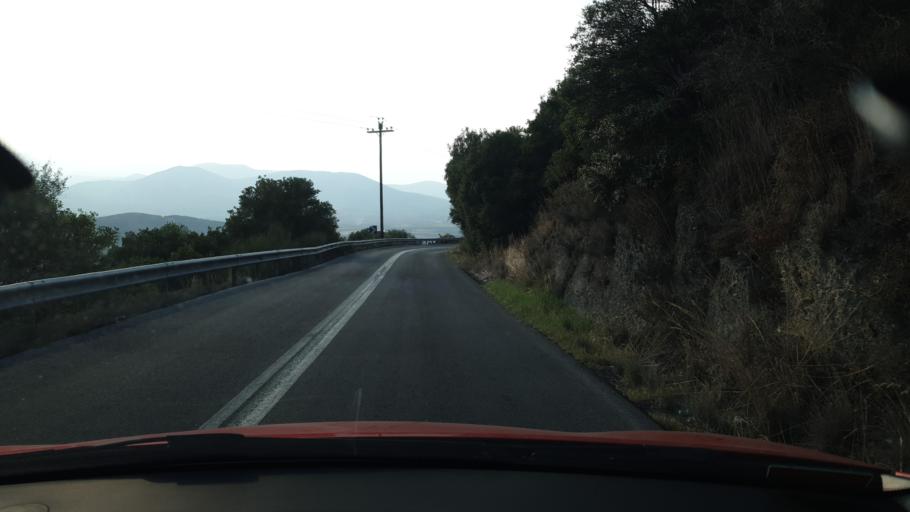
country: GR
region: Thessaly
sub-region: Nomos Magnisias
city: Pteleos
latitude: 39.0637
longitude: 22.9284
